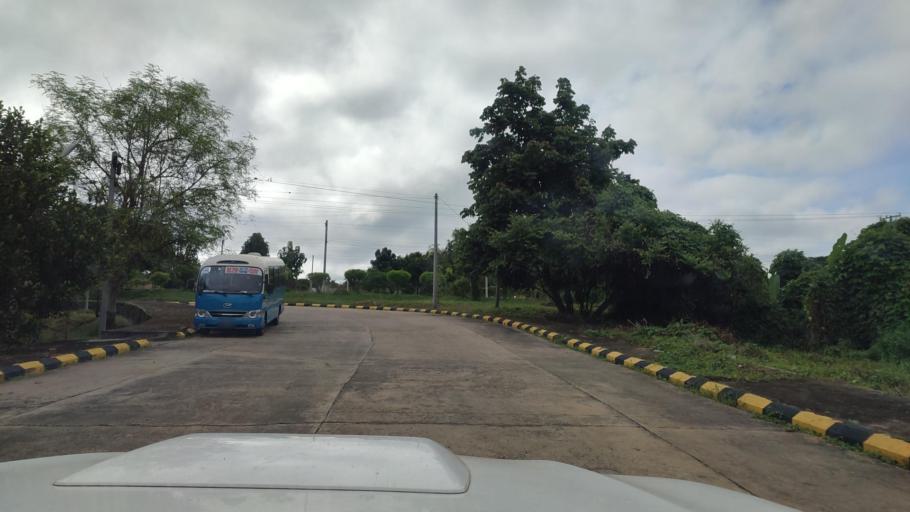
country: MM
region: Mandalay
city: Nay Pyi Taw
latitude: 19.7377
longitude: 96.0583
